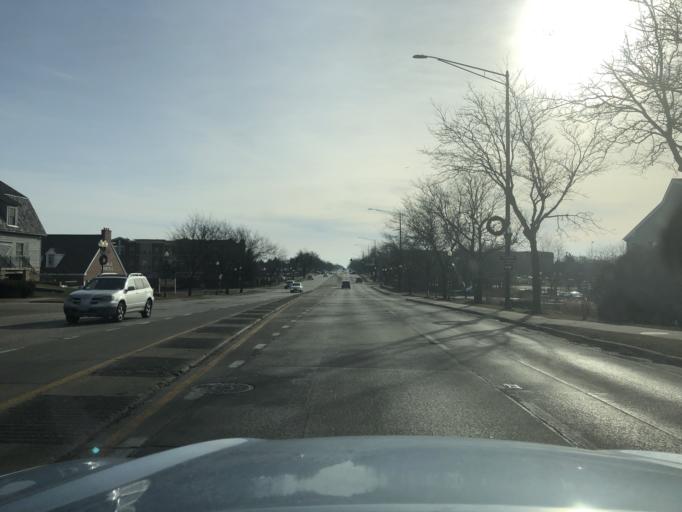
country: US
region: Illinois
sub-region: Cook County
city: Schaumburg
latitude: 42.0259
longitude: -88.0800
